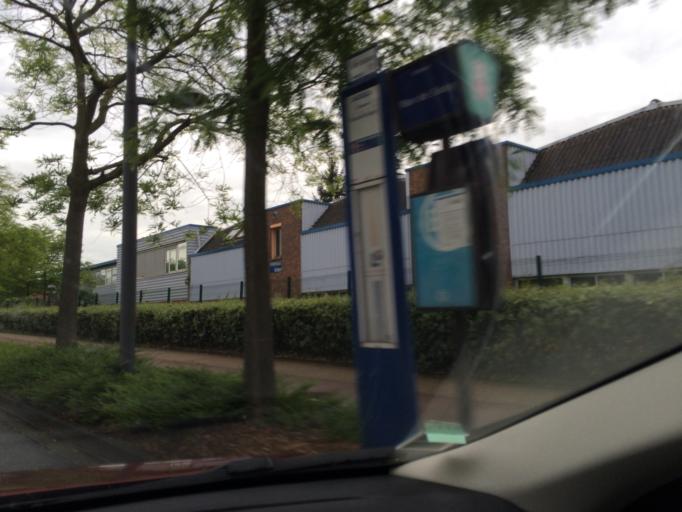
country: FR
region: Ile-de-France
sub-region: Departement du Val-d'Oise
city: Saint-Gratien
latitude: 48.9779
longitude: 2.2712
